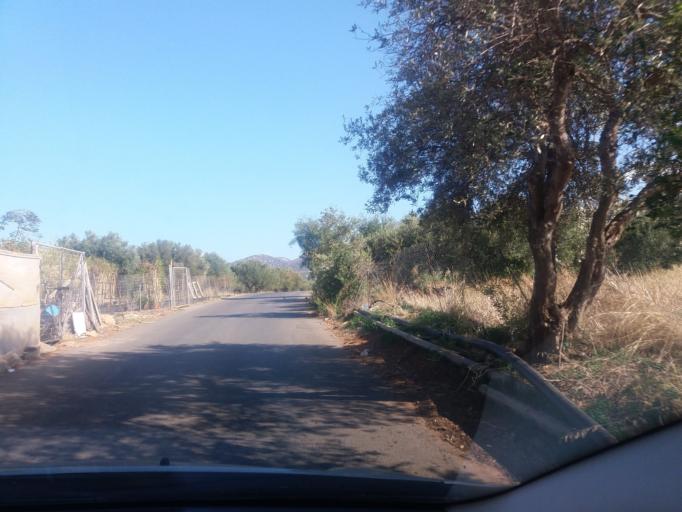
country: GR
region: Crete
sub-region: Nomos Irakleiou
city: Malia
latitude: 35.2911
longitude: 25.4862
